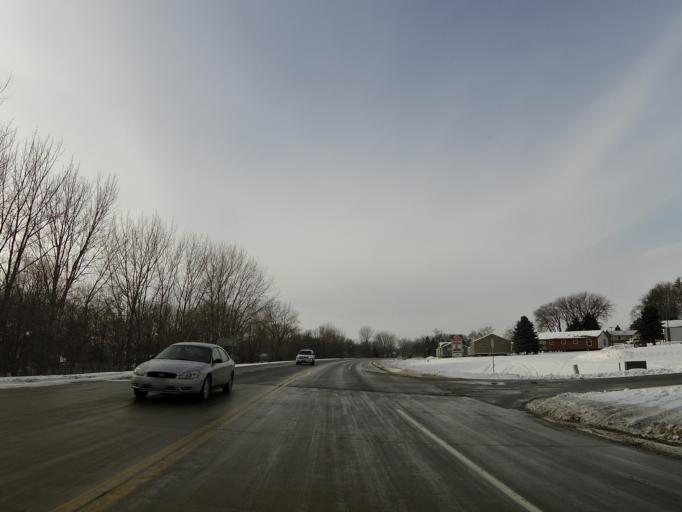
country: US
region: Minnesota
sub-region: McLeod County
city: Hutchinson
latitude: 44.8927
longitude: -94.3996
